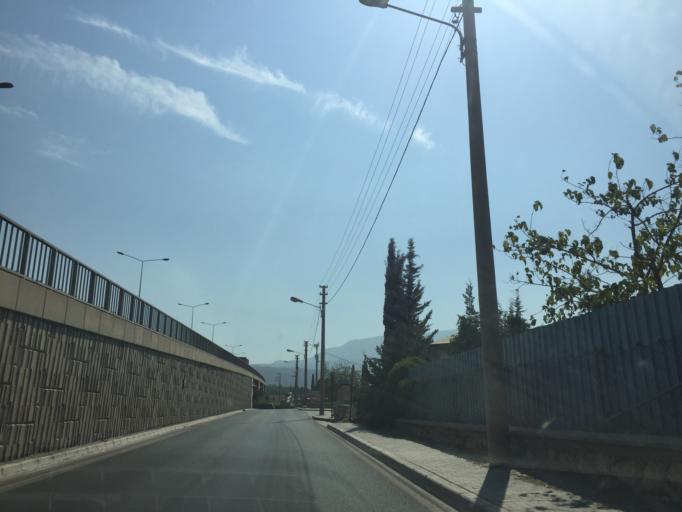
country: TR
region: Izmir
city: Bornova
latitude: 38.4531
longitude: 27.2637
